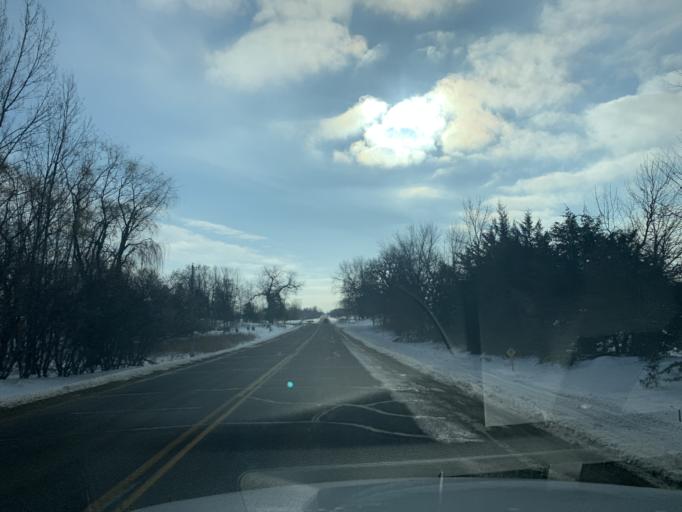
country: US
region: Minnesota
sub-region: Wright County
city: Buffalo
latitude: 45.1997
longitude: -93.8271
